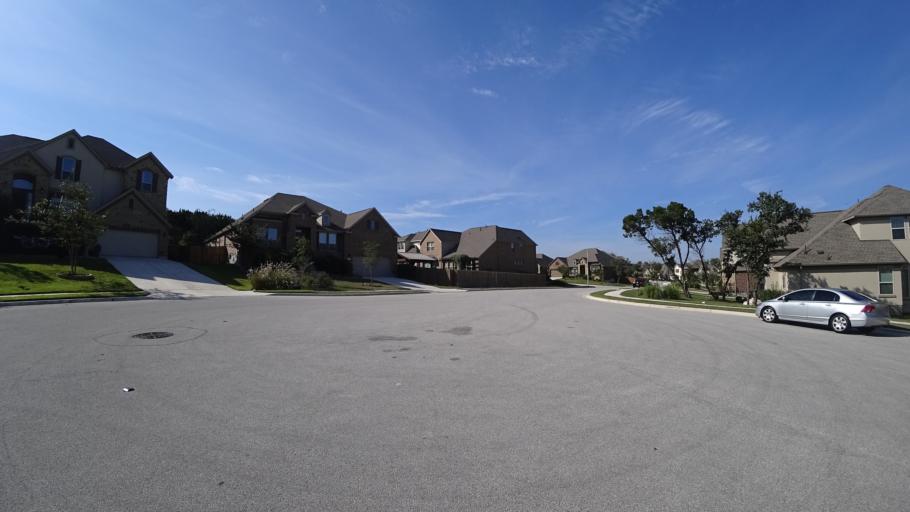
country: US
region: Texas
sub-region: Travis County
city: Barton Creek
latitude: 30.2293
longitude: -97.9078
